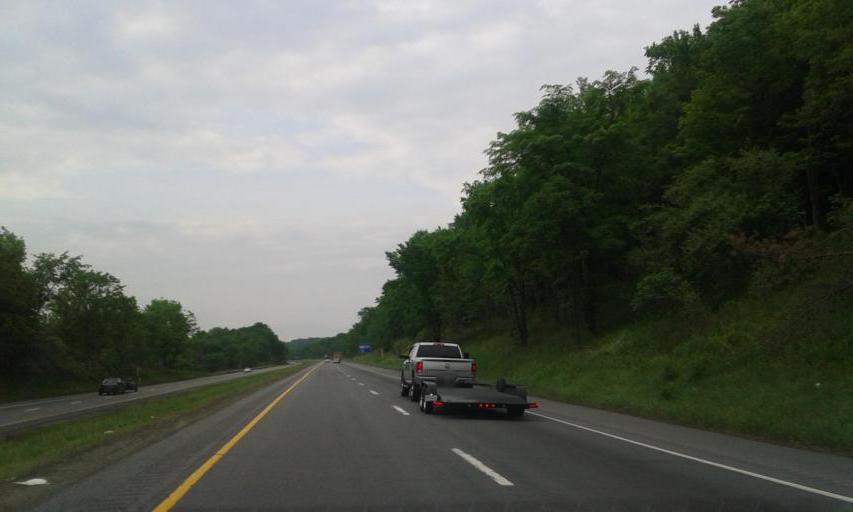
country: US
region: Pennsylvania
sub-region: Susquehanna County
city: Susquehanna
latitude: 41.8090
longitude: -75.6863
